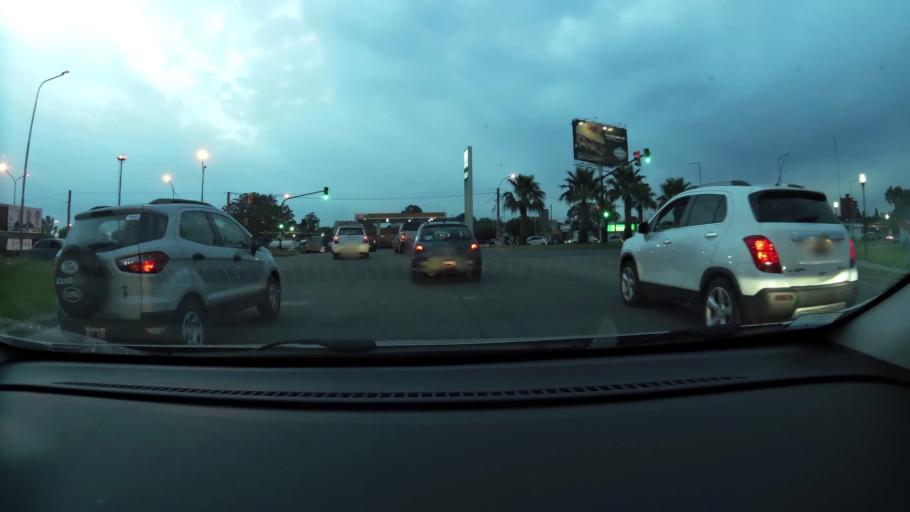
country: AR
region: Santa Fe
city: Granadero Baigorria
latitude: -32.8713
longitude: -60.6991
